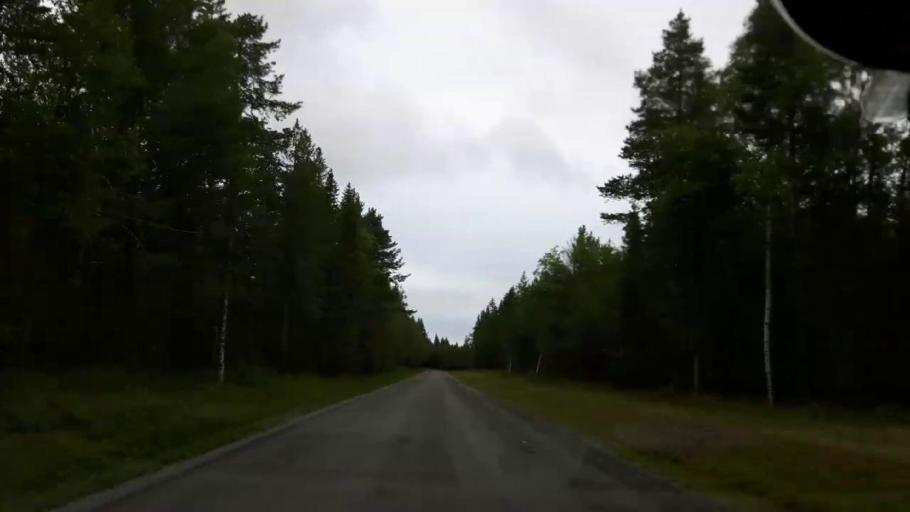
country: SE
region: Jaemtland
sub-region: OEstersunds Kommun
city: Ostersund
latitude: 63.1185
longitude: 14.5420
